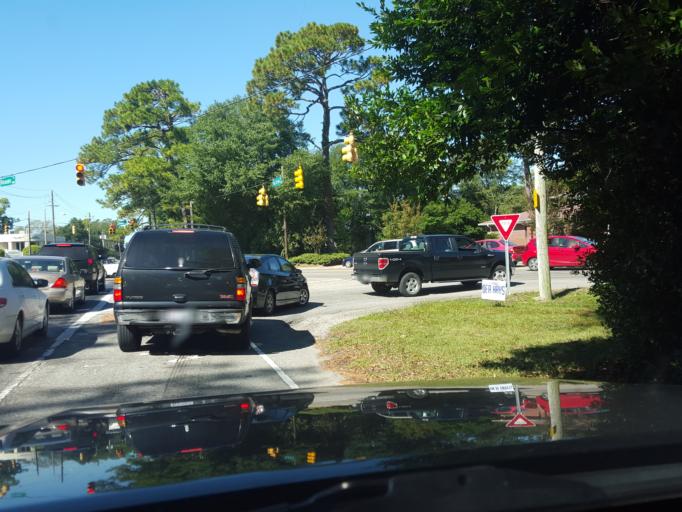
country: US
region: North Carolina
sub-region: New Hanover County
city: Seagate
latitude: 34.2094
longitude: -77.8808
